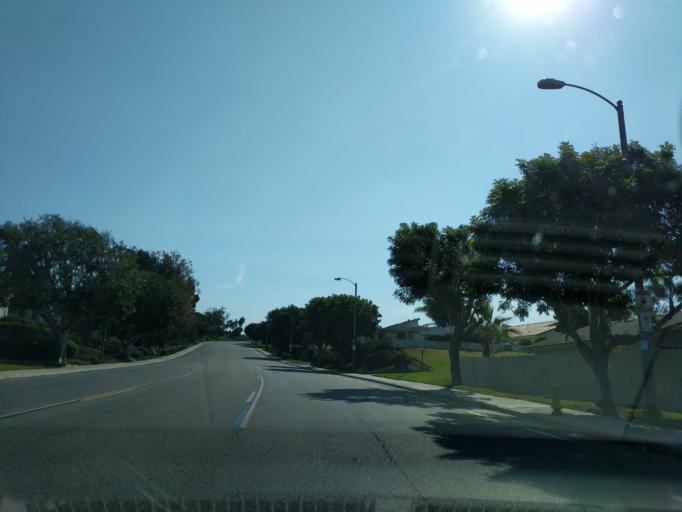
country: US
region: California
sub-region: San Diego County
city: Carlsbad
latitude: 33.1164
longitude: -117.3155
